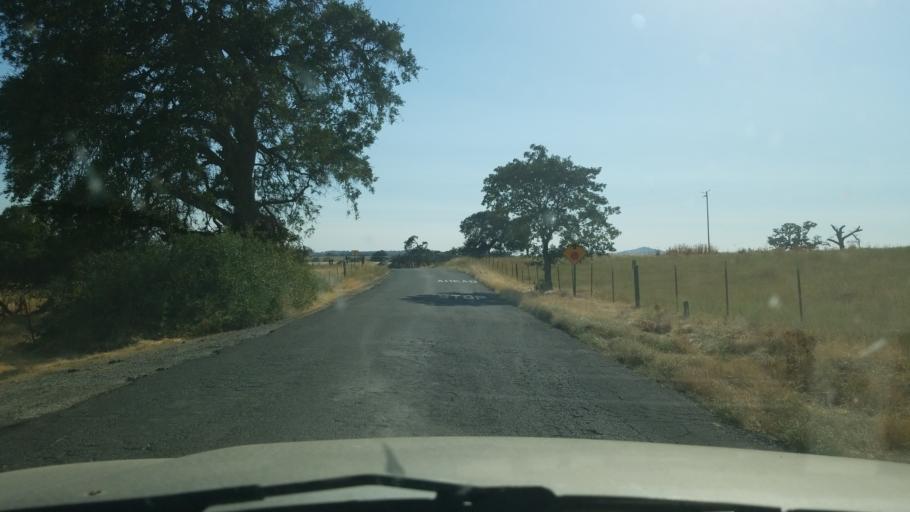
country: US
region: California
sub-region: Tuolumne County
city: Jamestown
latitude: 37.8327
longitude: -120.4769
